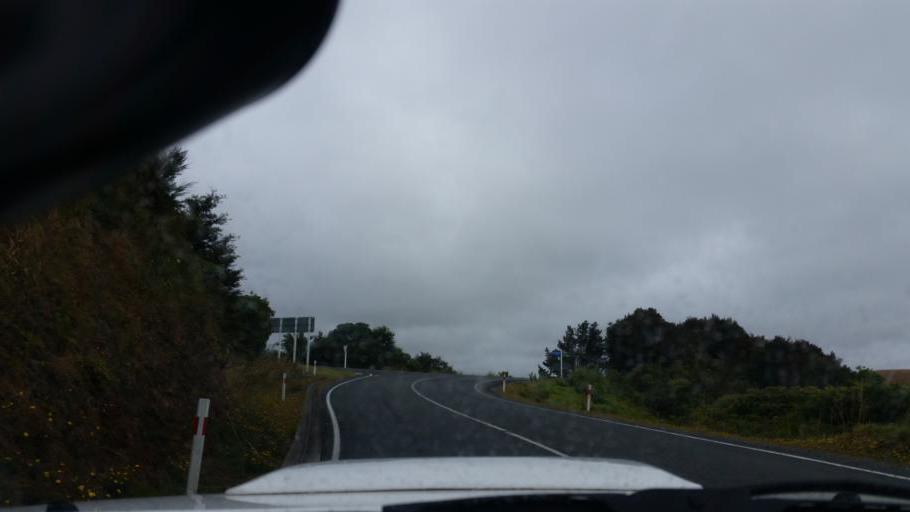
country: NZ
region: Auckland
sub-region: Auckland
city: Wellsford
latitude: -36.1327
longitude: 174.5289
